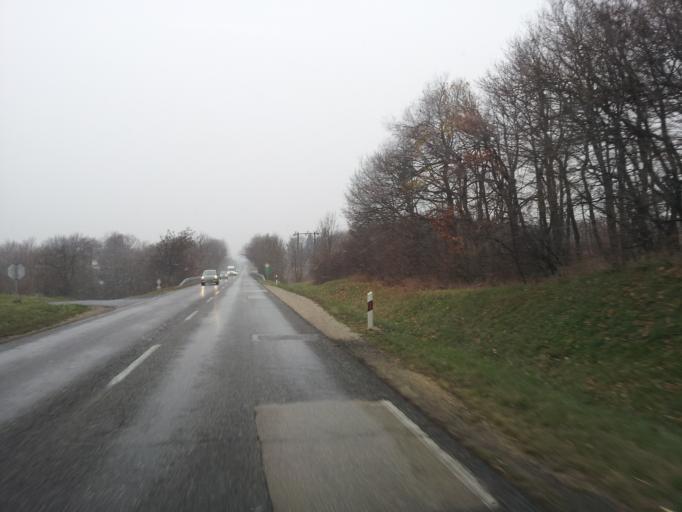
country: HU
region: Veszprem
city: Herend
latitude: 47.1431
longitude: 17.6969
